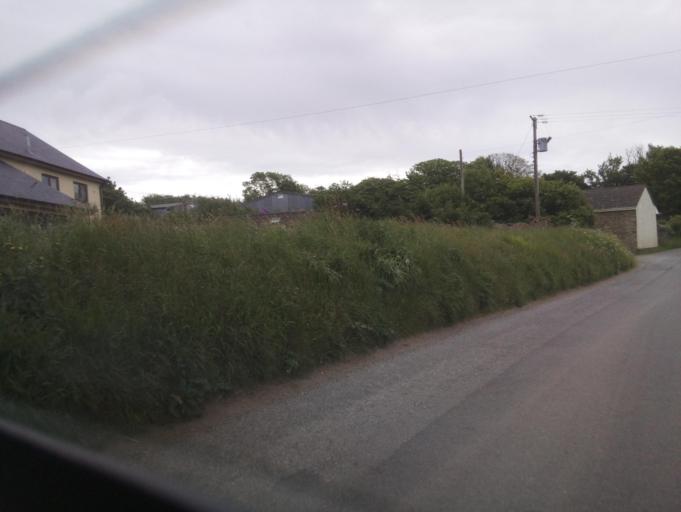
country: GB
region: England
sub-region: Devon
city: Dartmouth
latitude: 50.3336
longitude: -3.6474
